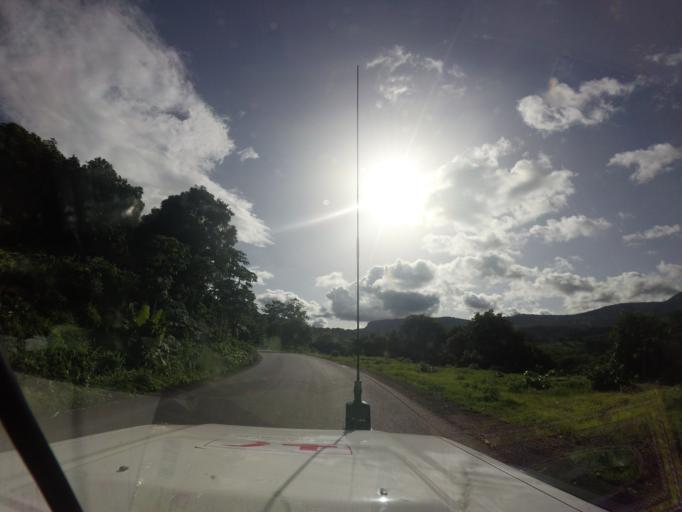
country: GN
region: Kindia
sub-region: Kindia
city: Kindia
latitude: 10.1782
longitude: -12.4773
